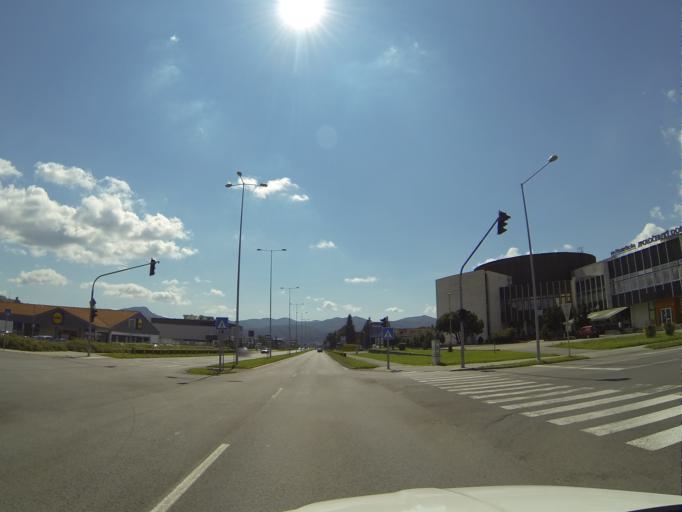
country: SK
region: Banskobystricky
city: Ziar nad Hronom
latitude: 48.5957
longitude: 18.8486
